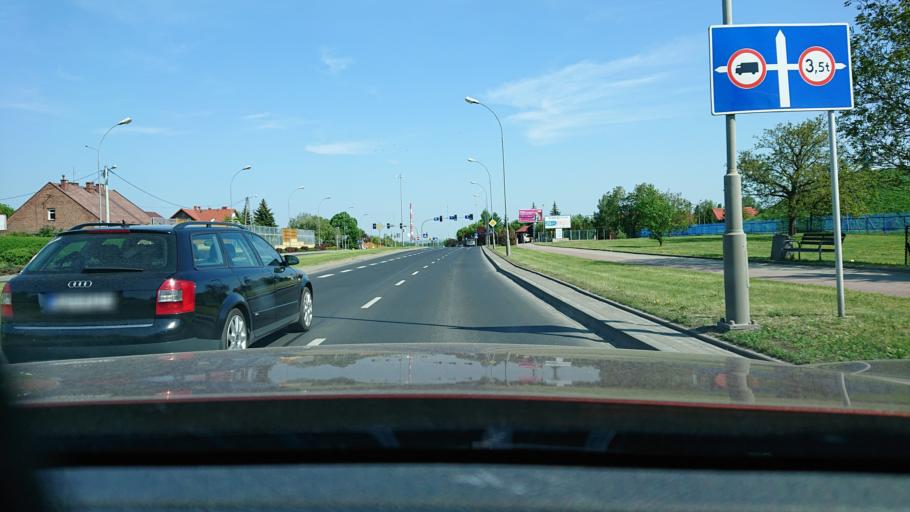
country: PL
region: Subcarpathian Voivodeship
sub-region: Rzeszow
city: Rzeszow
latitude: 50.0409
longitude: 22.0325
